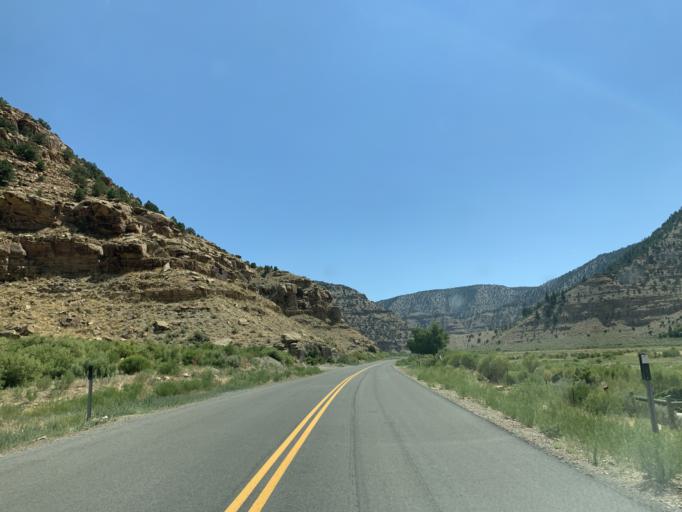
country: US
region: Utah
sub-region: Carbon County
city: East Carbon City
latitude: 39.8011
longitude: -110.3652
